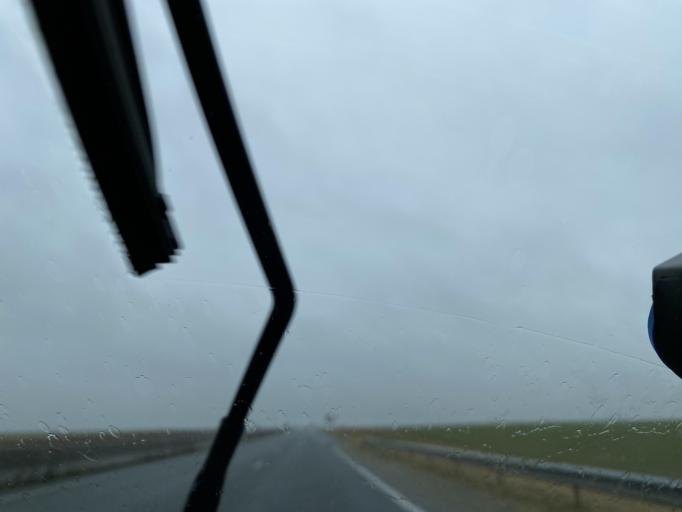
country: FR
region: Centre
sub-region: Departement d'Eure-et-Loir
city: Bailleau-l'Eveque
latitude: 48.5727
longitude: 1.4349
